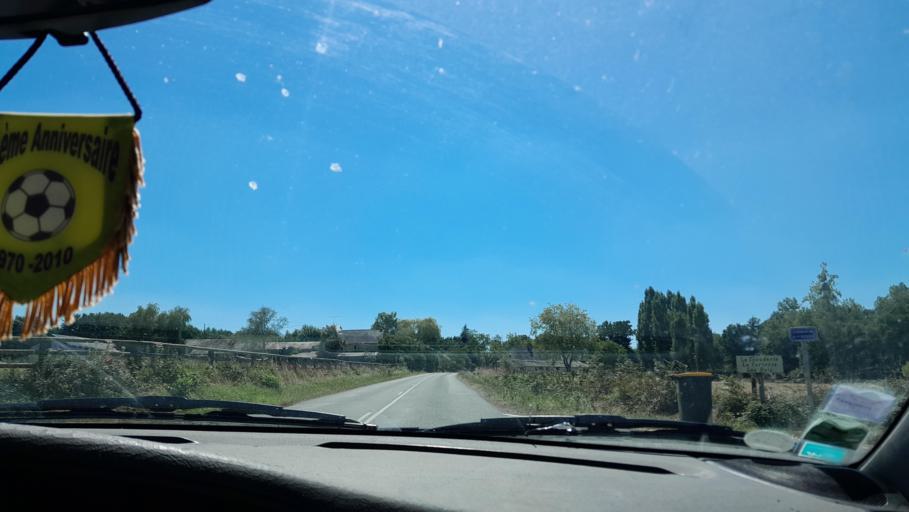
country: FR
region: Pays de la Loire
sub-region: Departement de la Mayenne
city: Ballots
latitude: 47.8898
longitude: -1.1172
